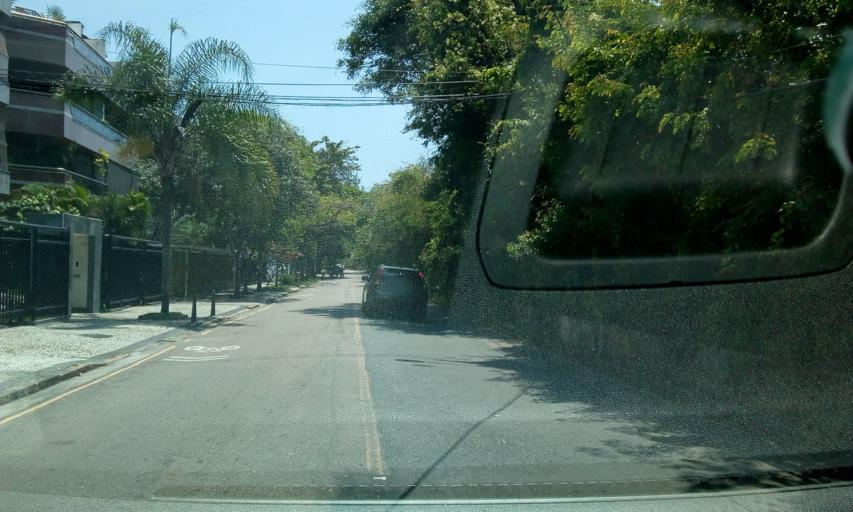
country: BR
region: Rio de Janeiro
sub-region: Nilopolis
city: Nilopolis
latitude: -23.0245
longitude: -43.4632
